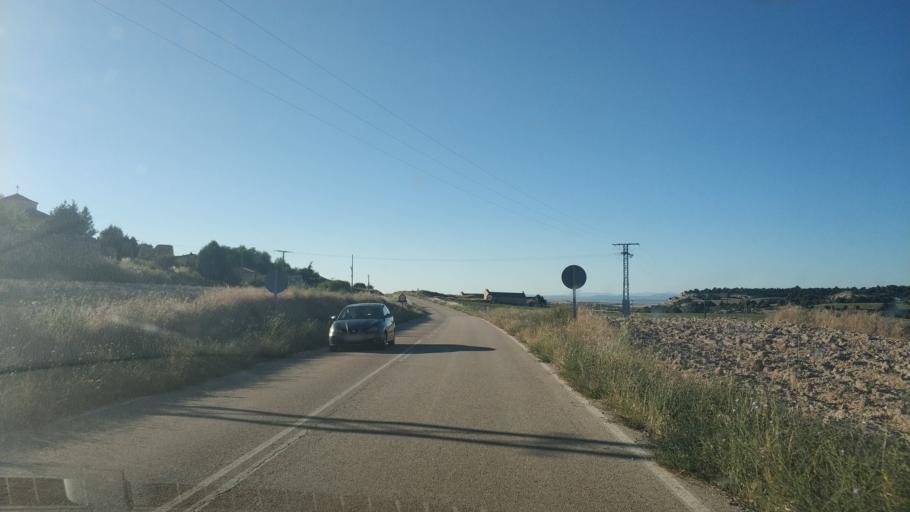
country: ES
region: Castille and Leon
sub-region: Provincia de Soria
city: Liceras
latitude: 41.4632
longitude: -3.2143
